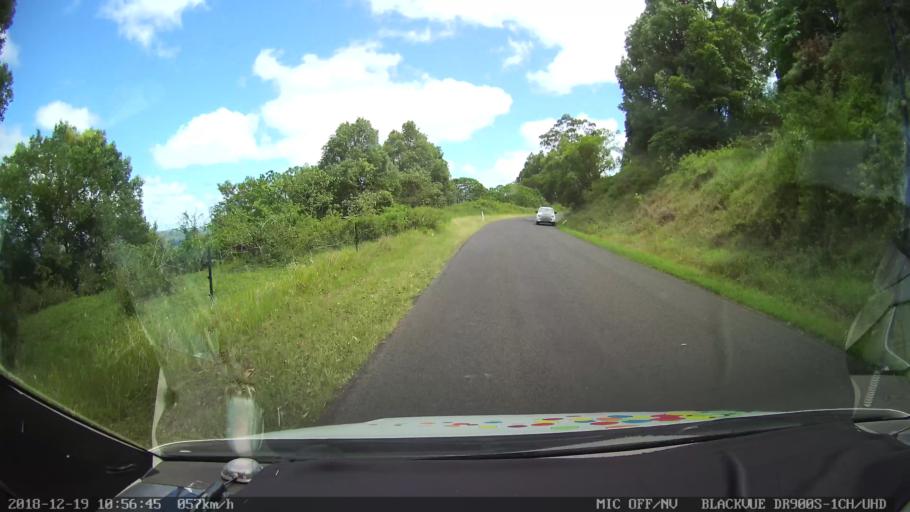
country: AU
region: New South Wales
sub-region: Lismore Municipality
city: Nimbin
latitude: -28.5924
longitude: 153.2612
